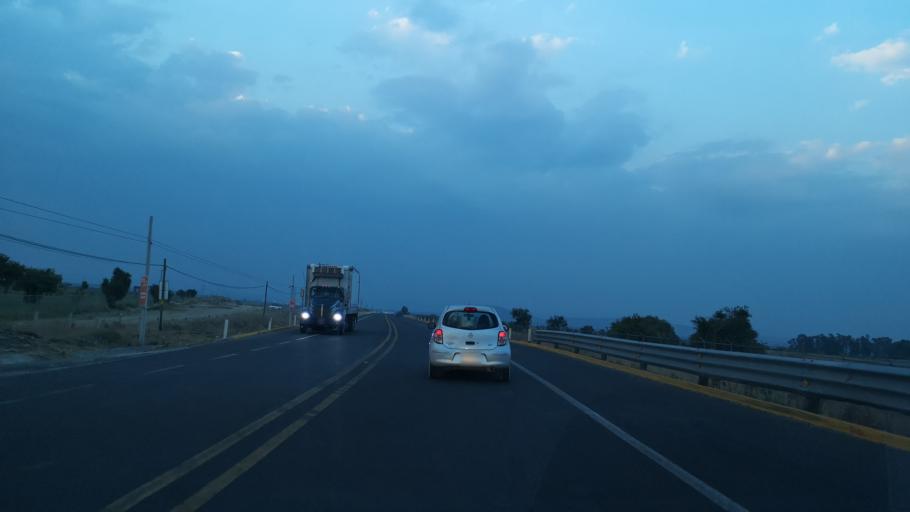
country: MX
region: Puebla
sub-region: Huejotzingo
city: Los Encinos
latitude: 19.1724
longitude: -98.3746
